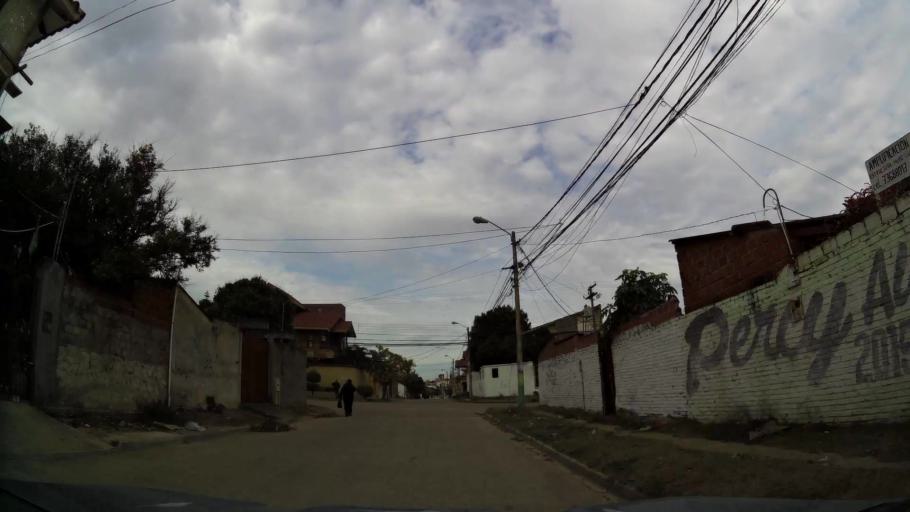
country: BO
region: Santa Cruz
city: Santa Cruz de la Sierra
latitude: -17.7710
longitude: -63.2008
